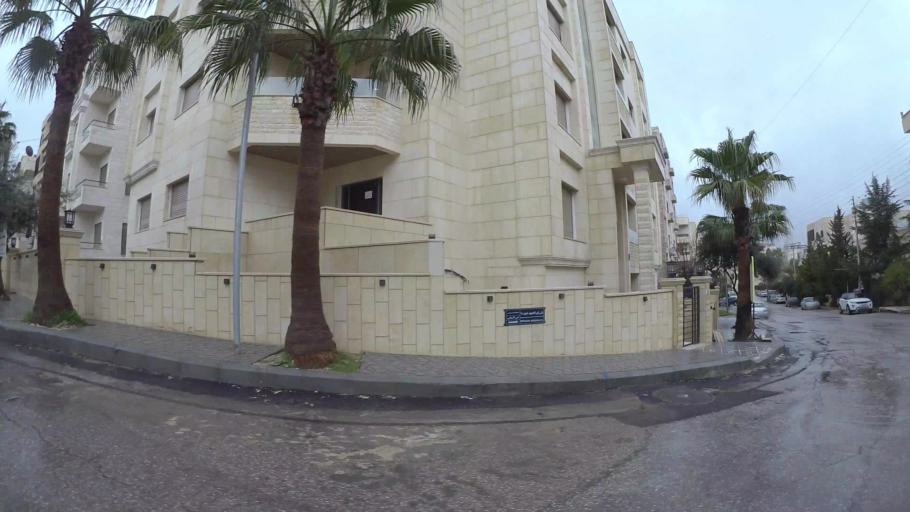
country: JO
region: Amman
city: Wadi as Sir
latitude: 31.9657
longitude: 35.8637
